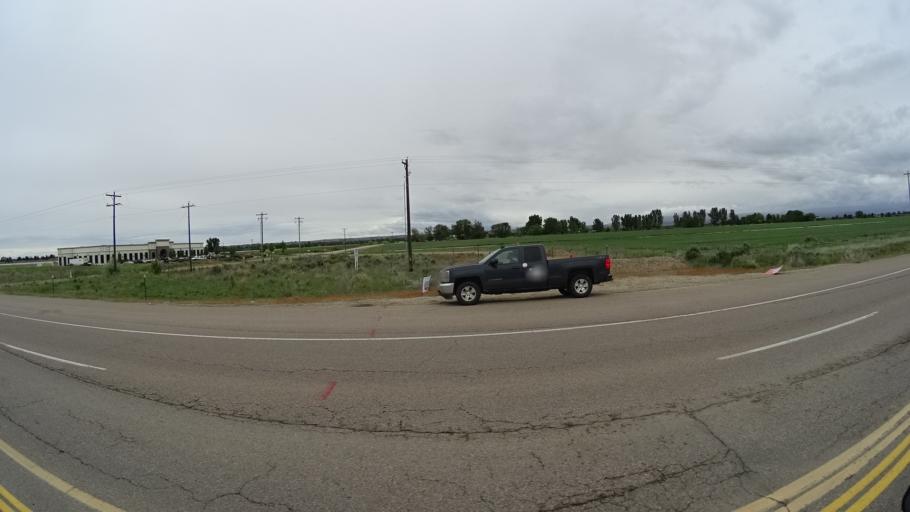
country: US
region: Idaho
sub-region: Ada County
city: Star
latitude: 43.6628
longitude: -116.4681
